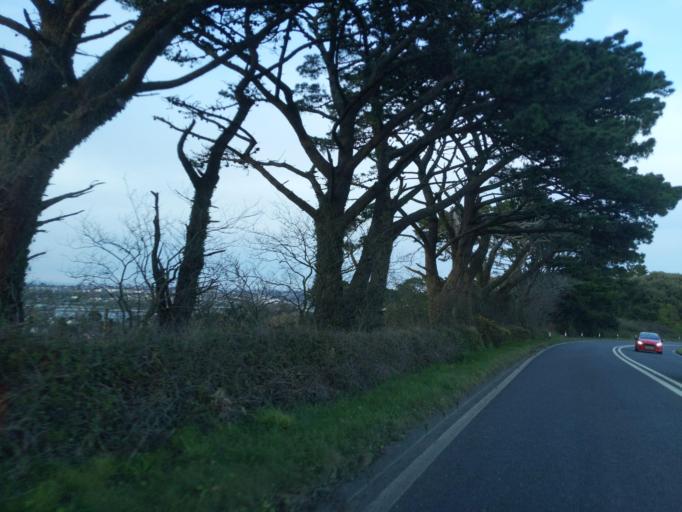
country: GB
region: England
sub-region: Cornwall
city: Torpoint
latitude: 50.3831
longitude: -4.2124
